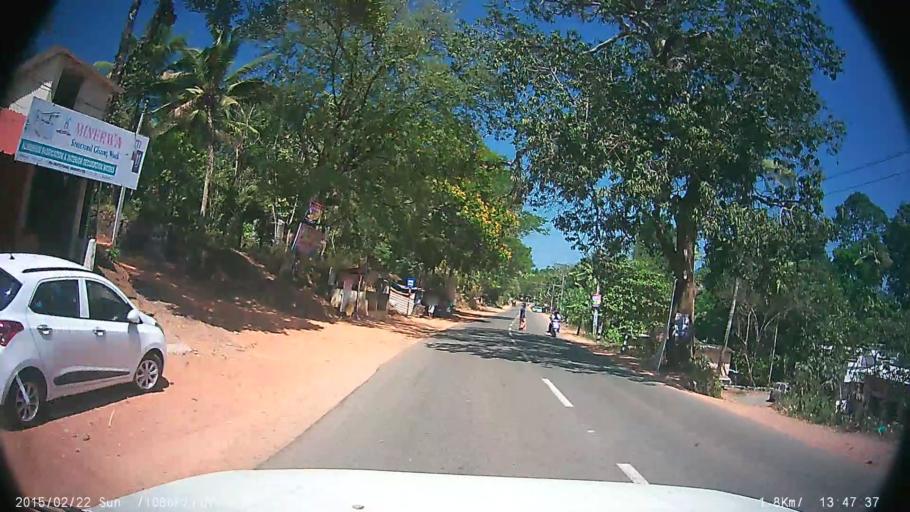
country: IN
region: Kerala
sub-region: Kottayam
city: Changanacheri
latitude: 9.4912
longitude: 76.6212
